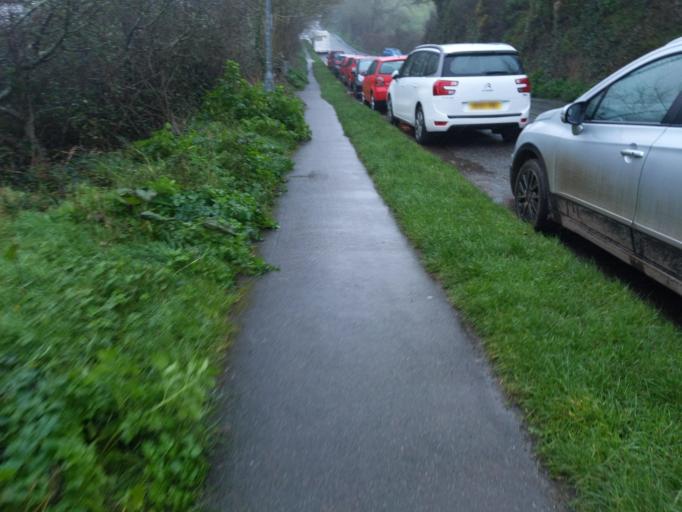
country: GB
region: England
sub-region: Cornwall
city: Millbrook
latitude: 50.3367
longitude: -4.2041
